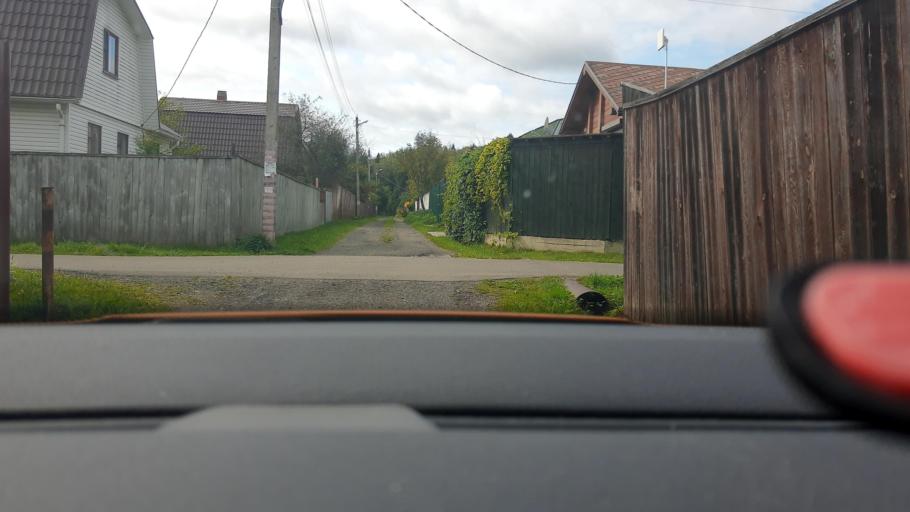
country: RU
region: Moskovskaya
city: Ashukino
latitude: 56.0897
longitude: 38.0218
